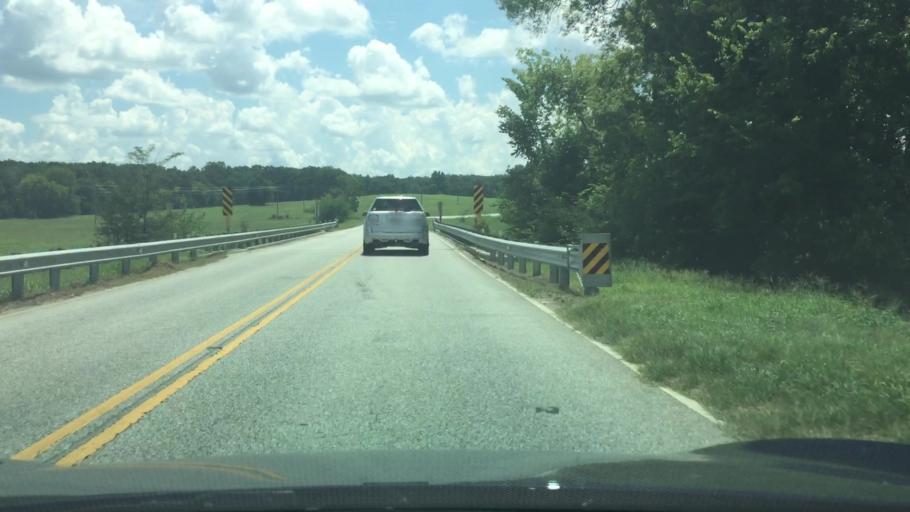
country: US
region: Alabama
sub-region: Montgomery County
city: Pike Road
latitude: 32.2560
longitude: -86.0966
